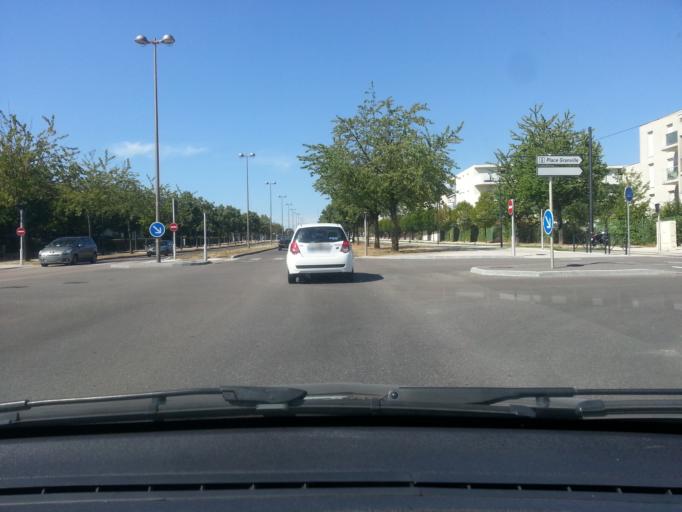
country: FR
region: Bourgogne
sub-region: Departement de la Cote-d'Or
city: Fontaine-les-Dijon
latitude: 47.3505
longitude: 5.0457
